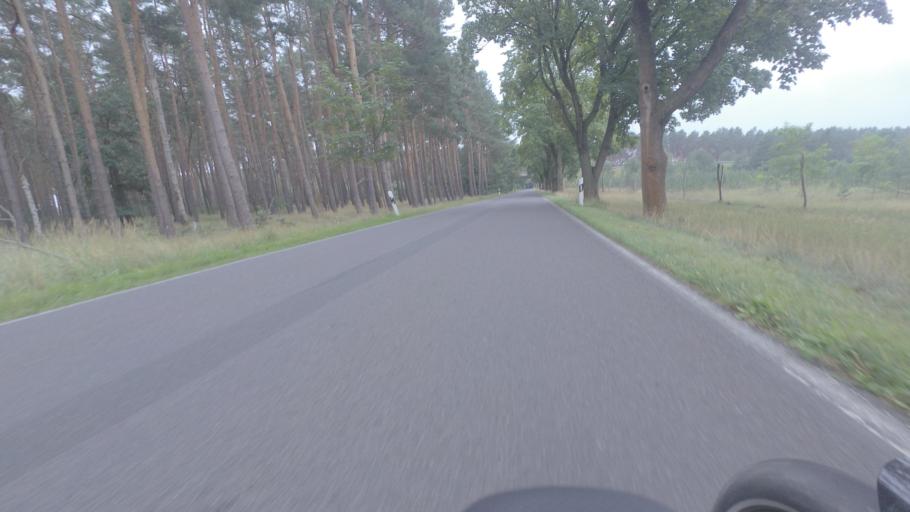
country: DE
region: Brandenburg
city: Luckenwalde
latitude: 52.1265
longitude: 13.1905
